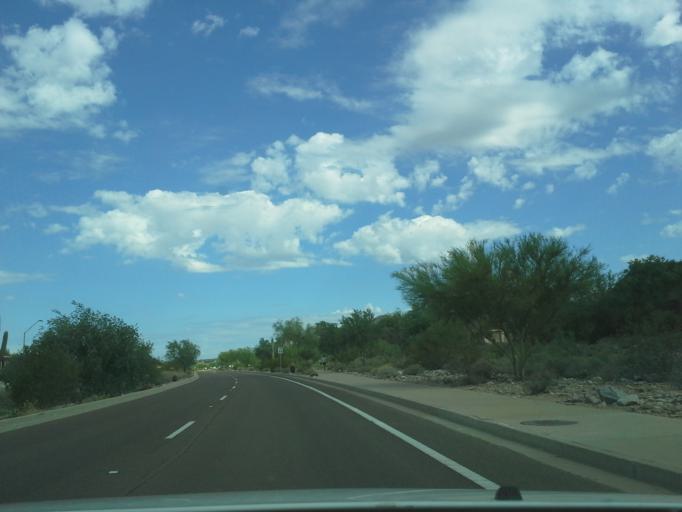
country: US
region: Arizona
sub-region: Maricopa County
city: Scottsdale
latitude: 33.6347
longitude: -111.8601
